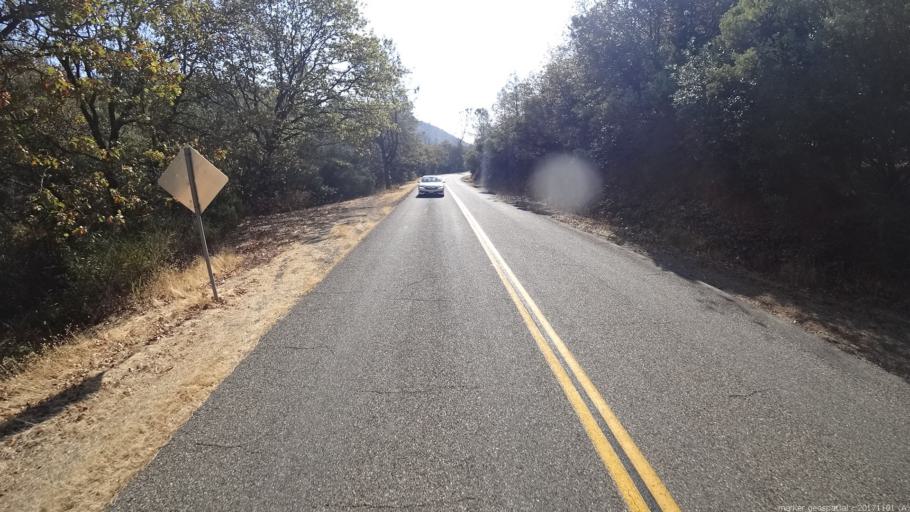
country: US
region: California
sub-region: Shasta County
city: Central Valley (historical)
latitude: 40.7116
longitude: -122.4061
